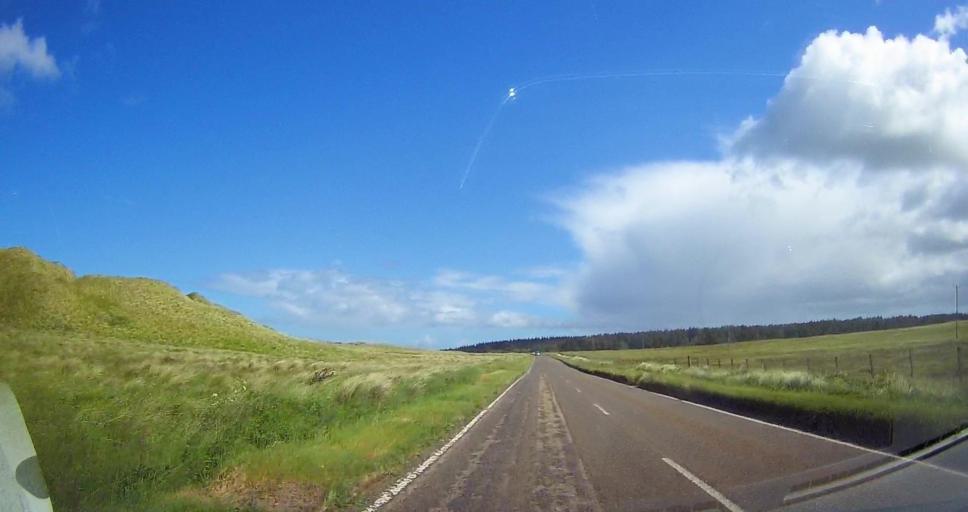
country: GB
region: Scotland
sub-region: Highland
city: Thurso
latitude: 58.6046
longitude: -3.3470
